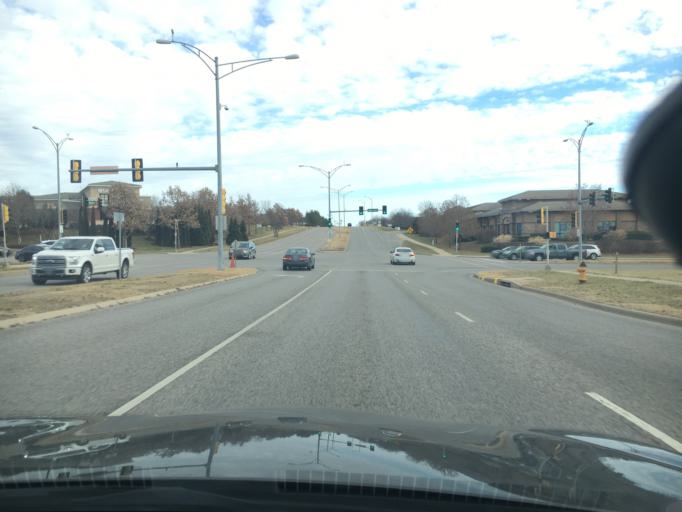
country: US
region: Kansas
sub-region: Johnson County
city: Leawood
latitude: 38.8546
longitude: -94.6501
